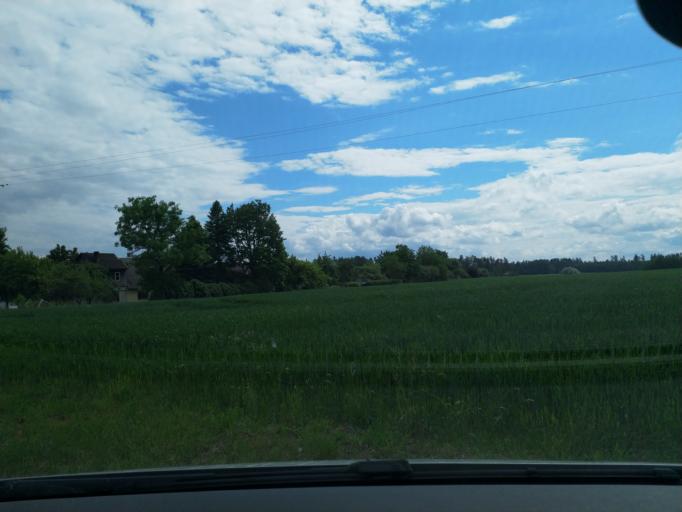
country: LV
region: Kuldigas Rajons
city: Kuldiga
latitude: 56.8376
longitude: 21.9417
